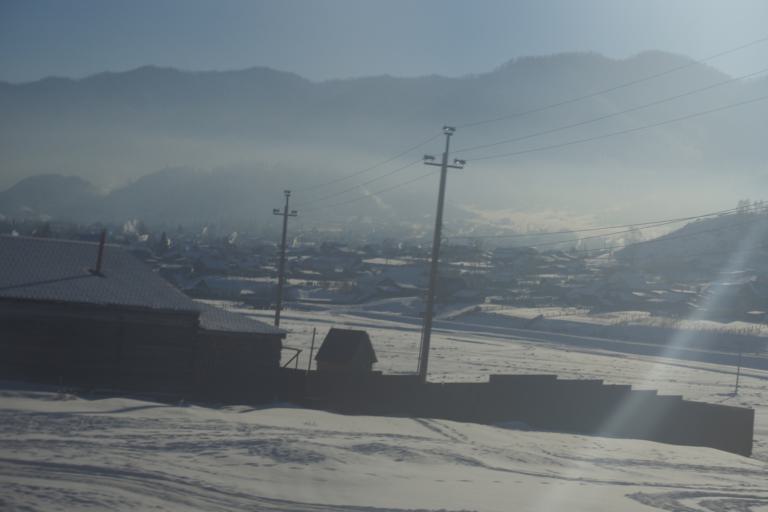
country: RU
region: Altay
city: Onguday
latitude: 50.7610
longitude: 86.1180
